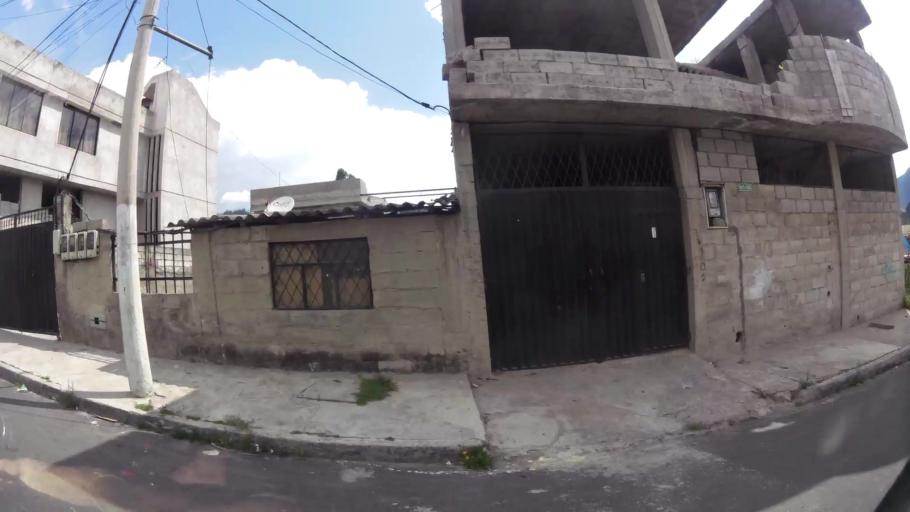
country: EC
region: Pichincha
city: Quito
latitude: -0.0945
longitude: -78.4553
